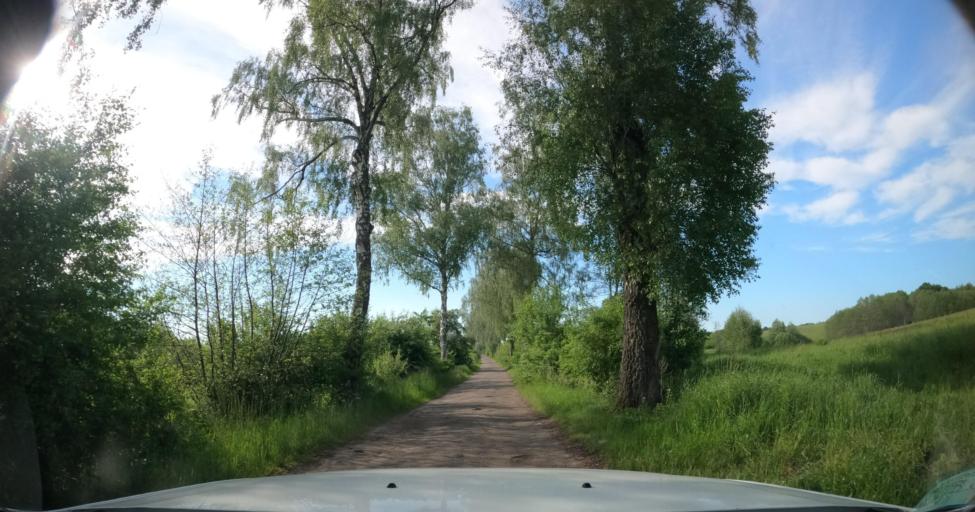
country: PL
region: Warmian-Masurian Voivodeship
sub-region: Powiat ostrodzki
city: Morag
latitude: 54.0507
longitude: 19.8919
